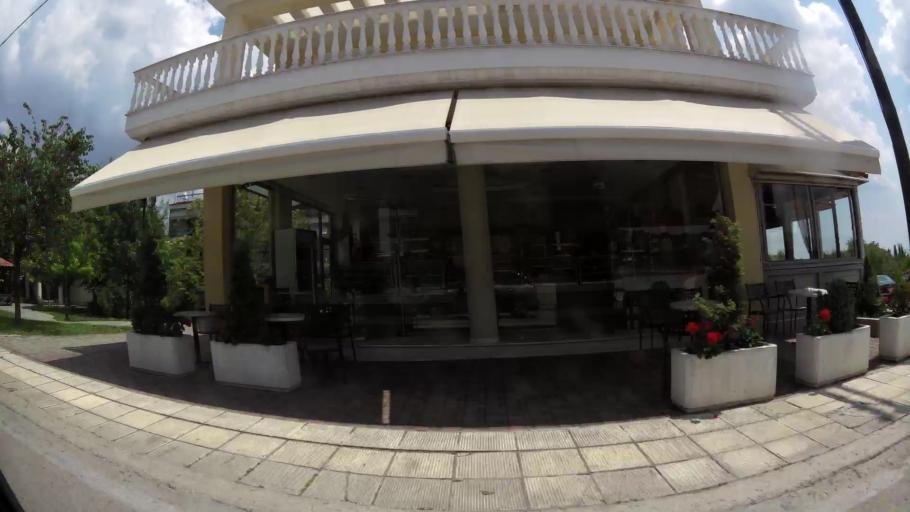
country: GR
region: West Macedonia
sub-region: Nomos Kozanis
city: Kozani
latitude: 40.2888
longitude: 21.7805
